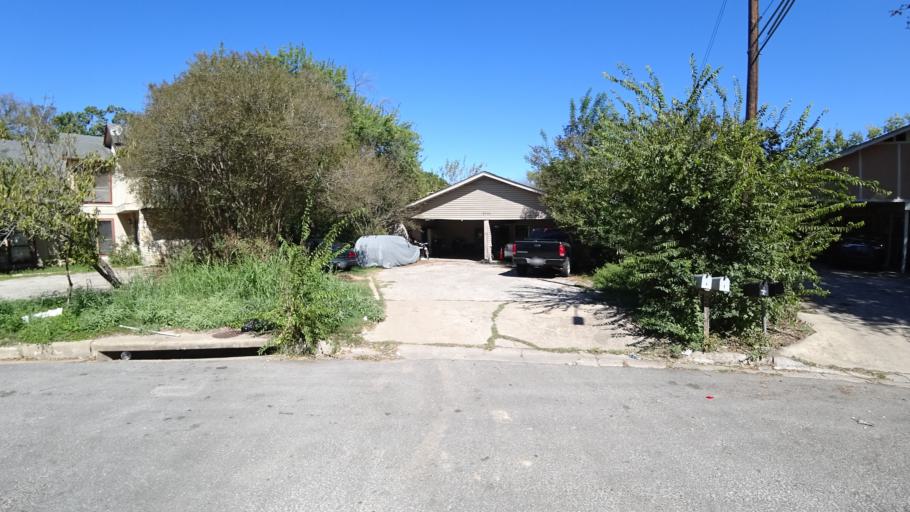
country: US
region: Texas
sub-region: Travis County
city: Austin
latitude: 30.2283
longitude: -97.7421
